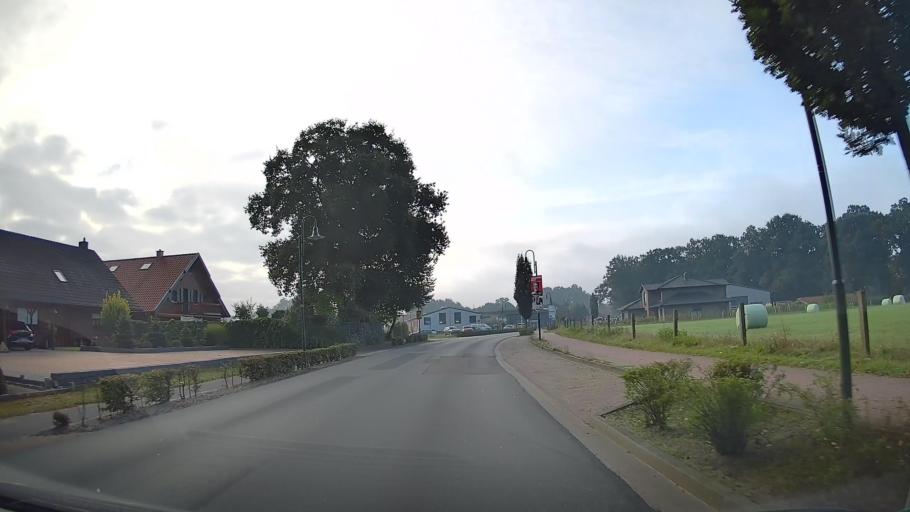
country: DE
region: Lower Saxony
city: Garrel
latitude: 52.9631
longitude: 8.0252
